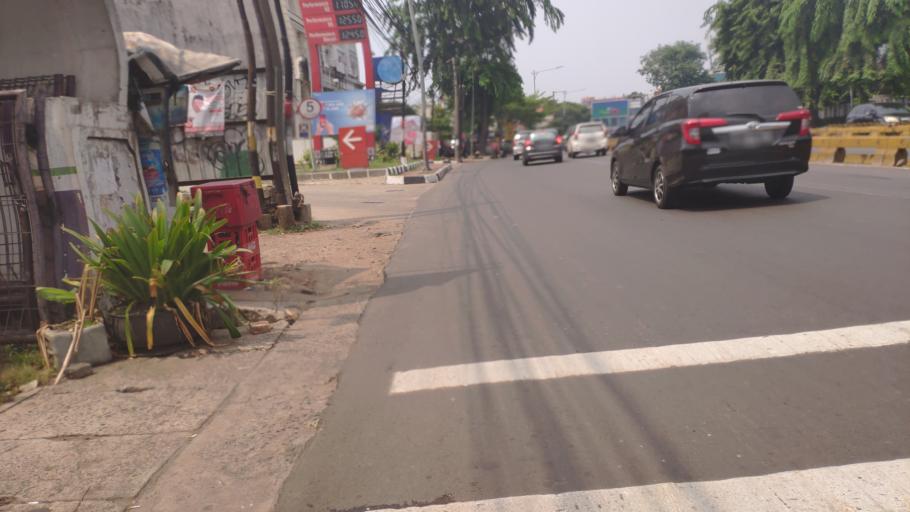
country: ID
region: Jakarta Raya
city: Jakarta
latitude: -6.2647
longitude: 106.8304
